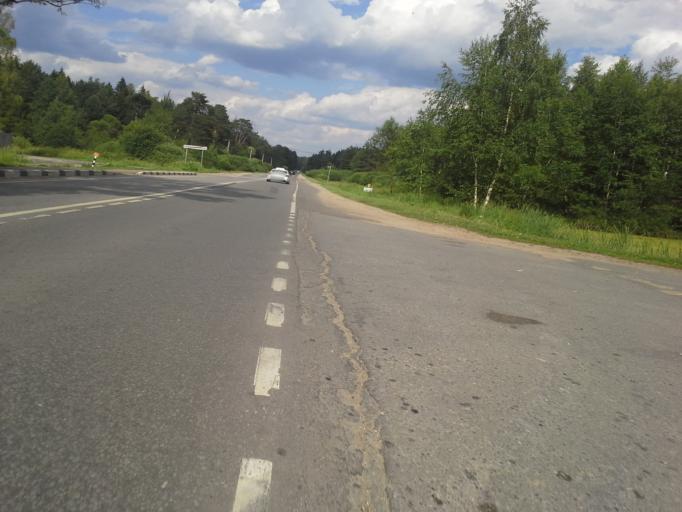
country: RU
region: Moskovskaya
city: Naro-Fominsk
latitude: 55.3982
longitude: 36.7753
